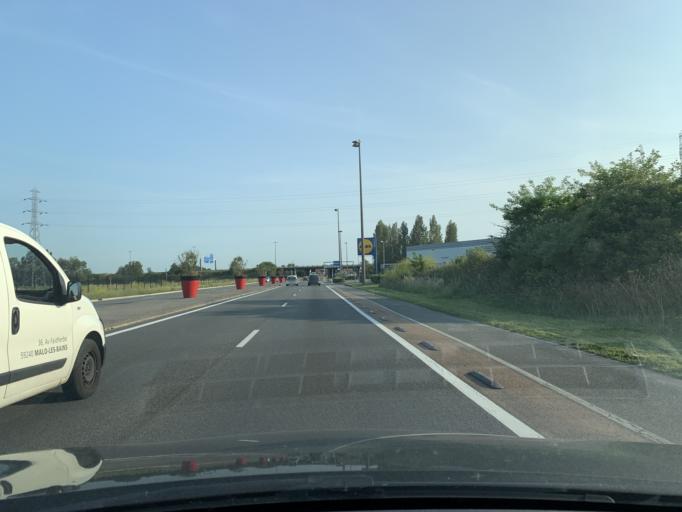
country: FR
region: Nord-Pas-de-Calais
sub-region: Departement du Nord
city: Coudekerque-Branche
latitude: 51.0303
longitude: 2.4058
